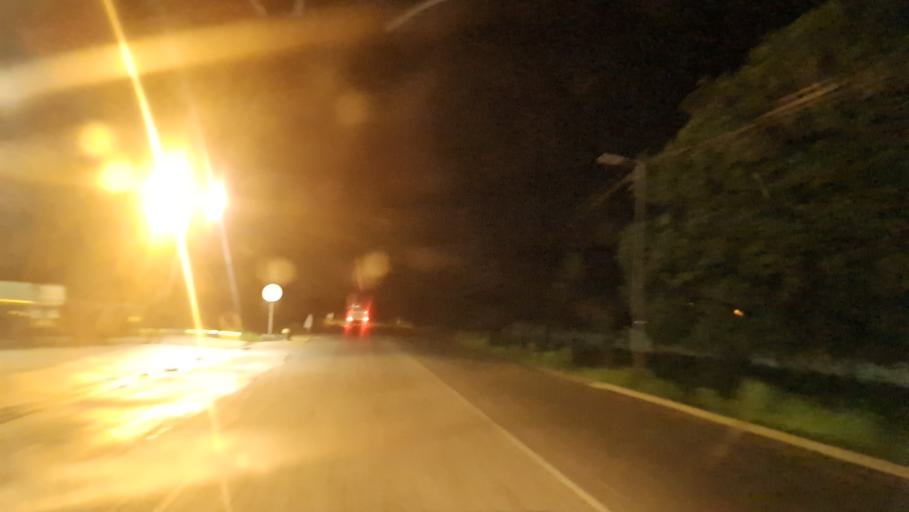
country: MZ
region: Nampula
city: Nacala
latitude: -14.6540
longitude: 40.6833
